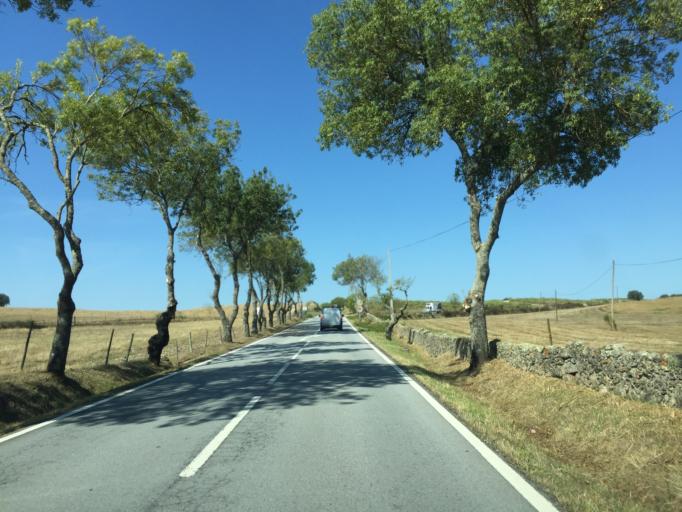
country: PT
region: Portalegre
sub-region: Castelo de Vide
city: Castelo de Vide
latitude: 39.4319
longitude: -7.5043
